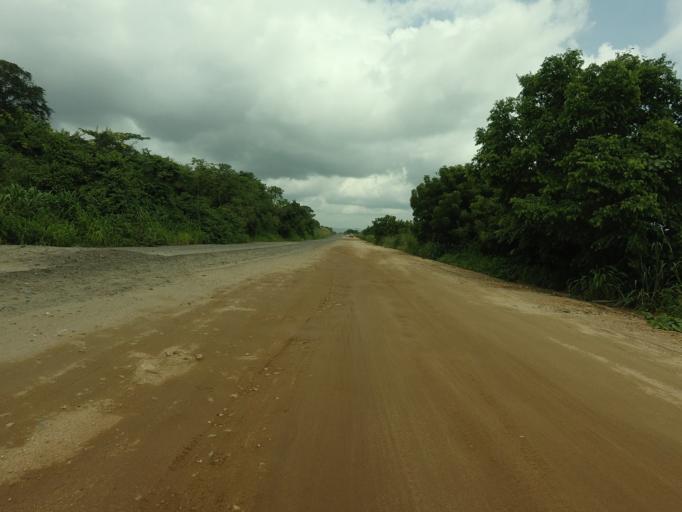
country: GH
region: Volta
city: Ho
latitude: 6.6582
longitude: 0.3039
